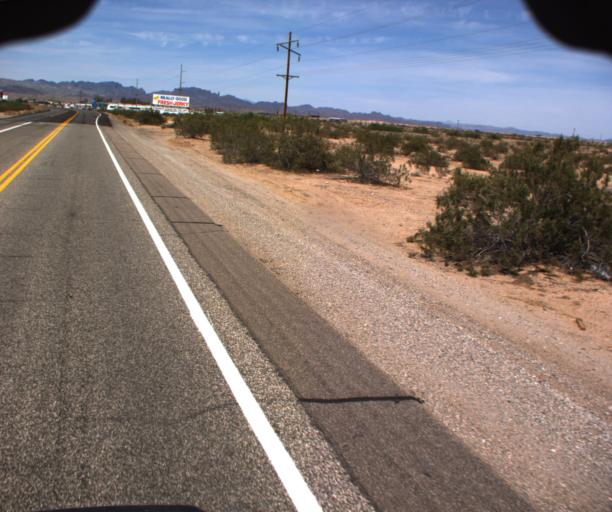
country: US
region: Arizona
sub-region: La Paz County
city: Parker
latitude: 34.1307
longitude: -114.2797
